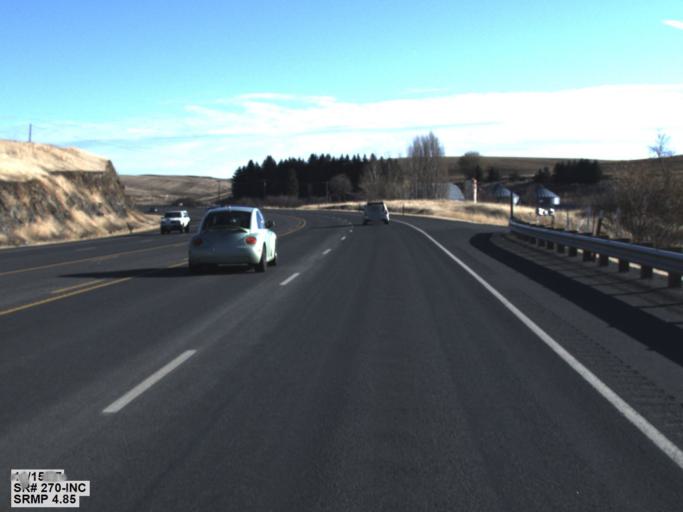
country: US
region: Washington
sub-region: Whitman County
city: Pullman
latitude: 46.7212
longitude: -117.1373
